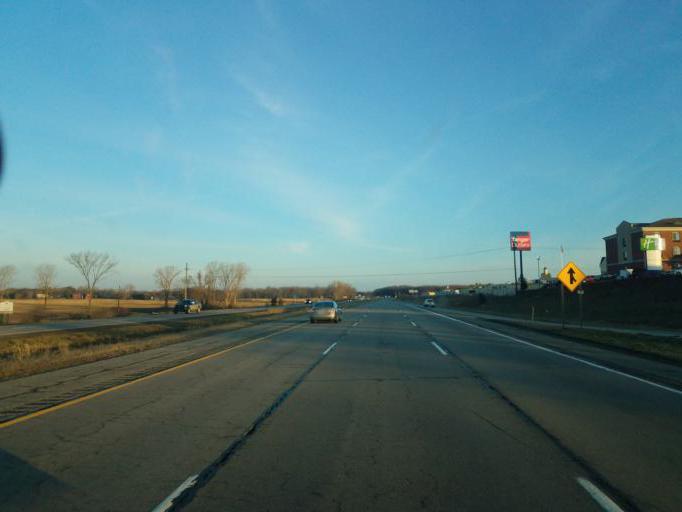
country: US
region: Michigan
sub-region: Livingston County
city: Howell
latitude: 42.6175
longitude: -83.9942
